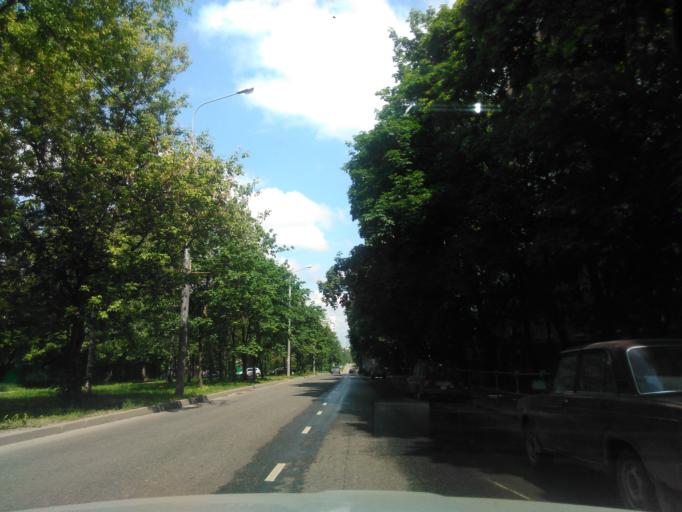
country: RU
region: Moscow
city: Vagonoremont
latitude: 55.8909
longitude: 37.5367
